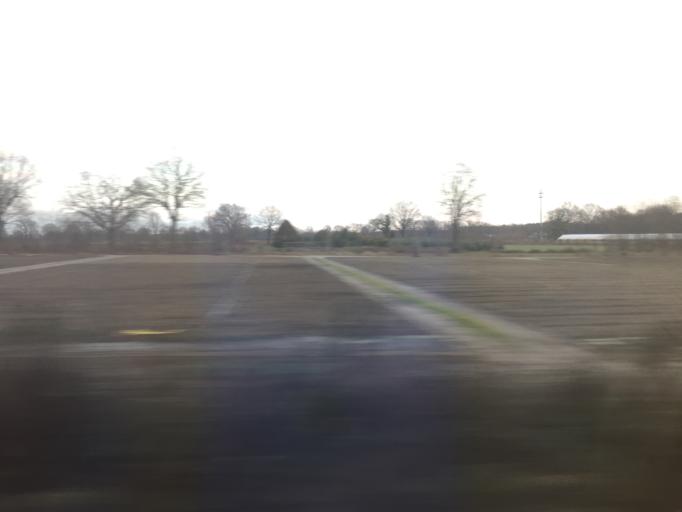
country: DE
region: Schleswig-Holstein
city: Prisdorf
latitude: 53.6826
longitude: 9.7436
